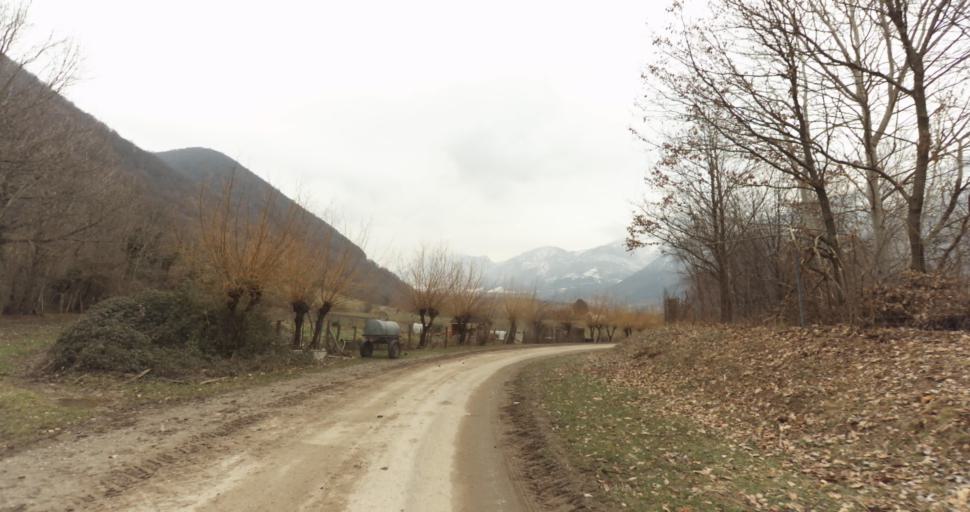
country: FR
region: Rhone-Alpes
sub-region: Departement de l'Isere
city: Vif
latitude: 45.0435
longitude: 5.6785
